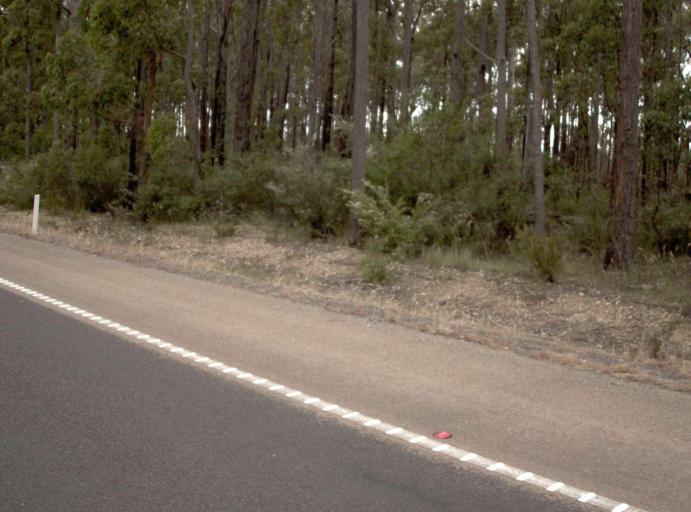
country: AU
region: Victoria
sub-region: East Gippsland
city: Lakes Entrance
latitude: -37.7325
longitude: 147.9420
